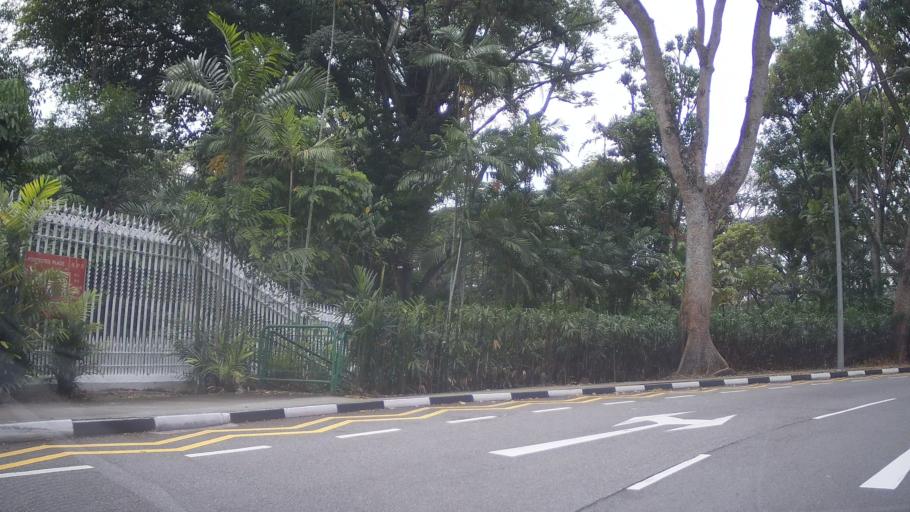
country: SG
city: Singapore
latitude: 1.3014
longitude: 103.8436
